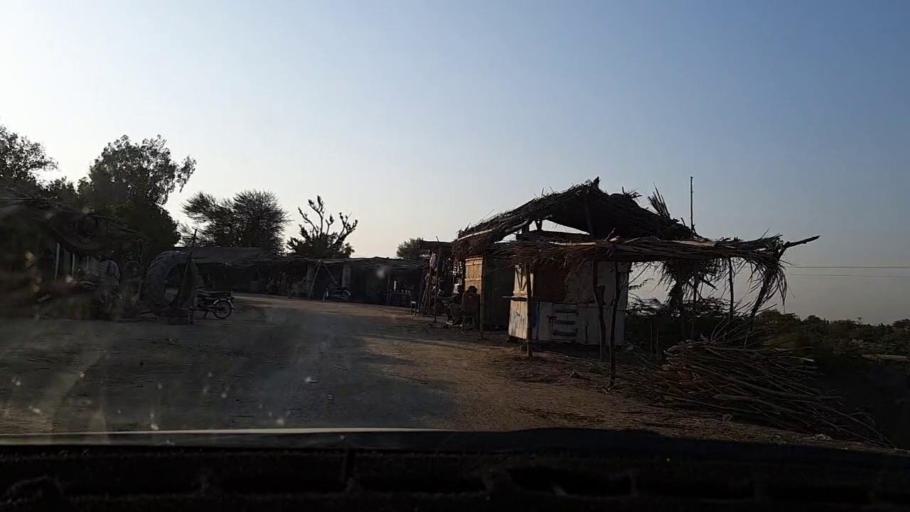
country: PK
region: Sindh
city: Tando Mittha Khan
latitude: 25.8561
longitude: 69.2729
